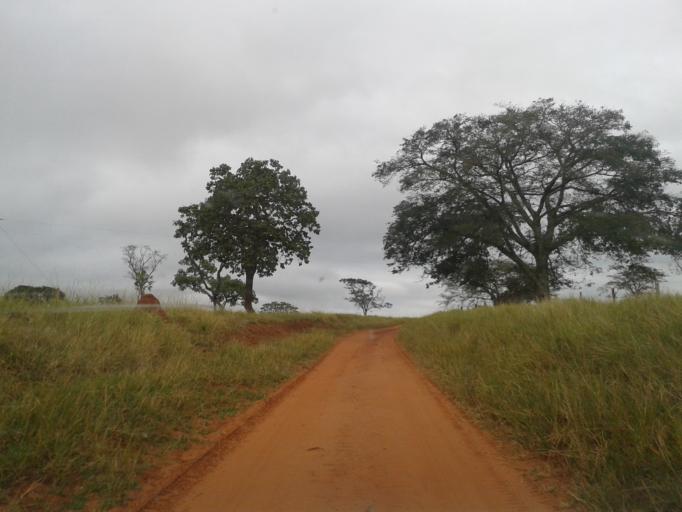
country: BR
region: Minas Gerais
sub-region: Campina Verde
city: Campina Verde
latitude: -19.4107
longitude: -49.6497
